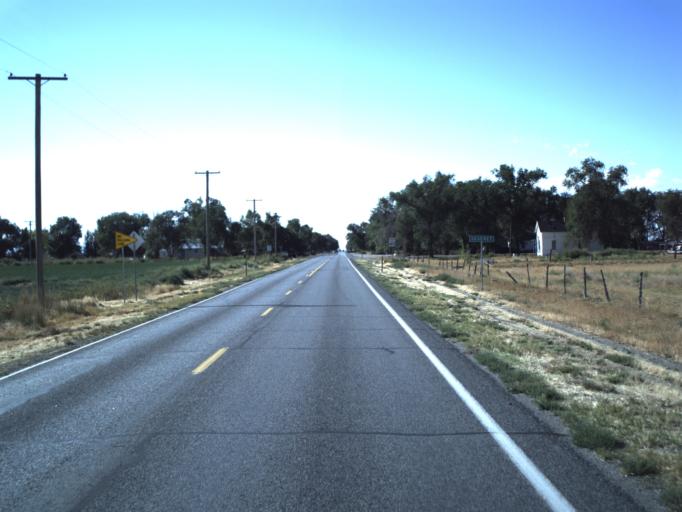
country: US
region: Utah
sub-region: Millard County
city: Delta
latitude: 39.2961
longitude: -112.6526
